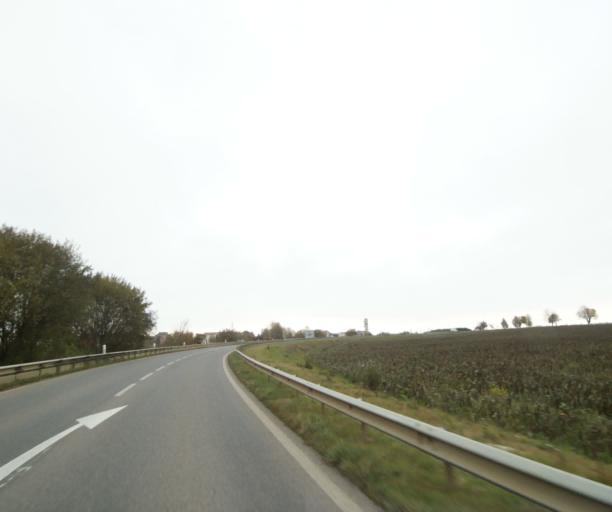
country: FR
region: Lorraine
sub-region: Departement de Meurthe-et-Moselle
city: Moutiers
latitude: 49.2466
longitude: 5.9560
